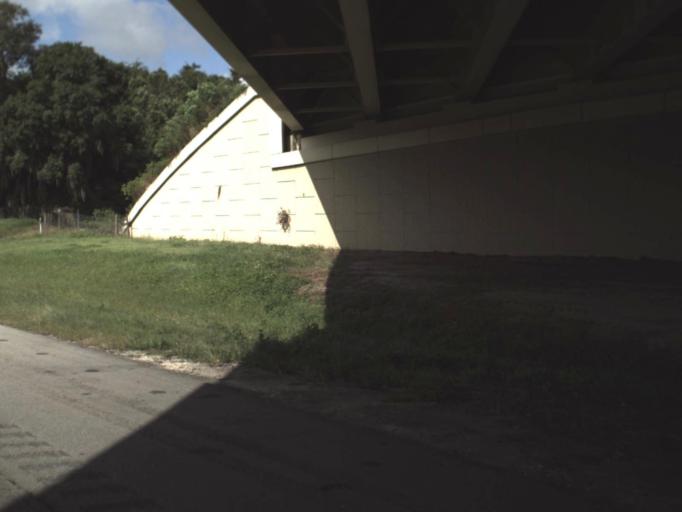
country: US
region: Florida
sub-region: Polk County
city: Winston
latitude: 28.0549
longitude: -82.0115
